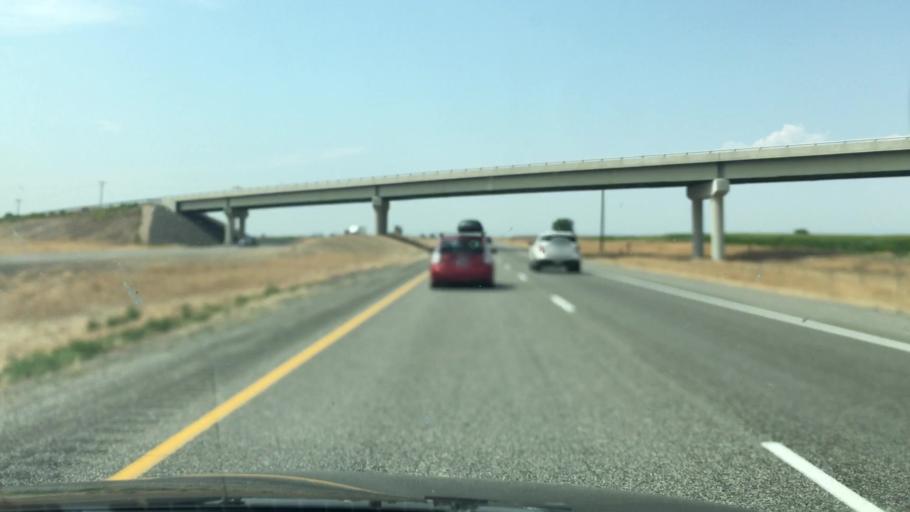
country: US
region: Idaho
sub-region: Gooding County
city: Wendell
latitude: 42.7966
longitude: -114.7538
